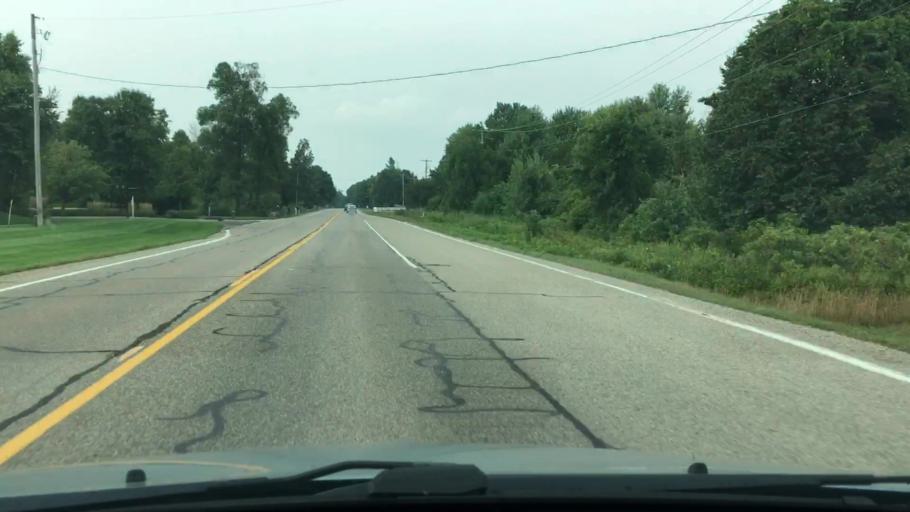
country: US
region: Michigan
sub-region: Ottawa County
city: Hudsonville
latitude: 42.8907
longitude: -85.9016
